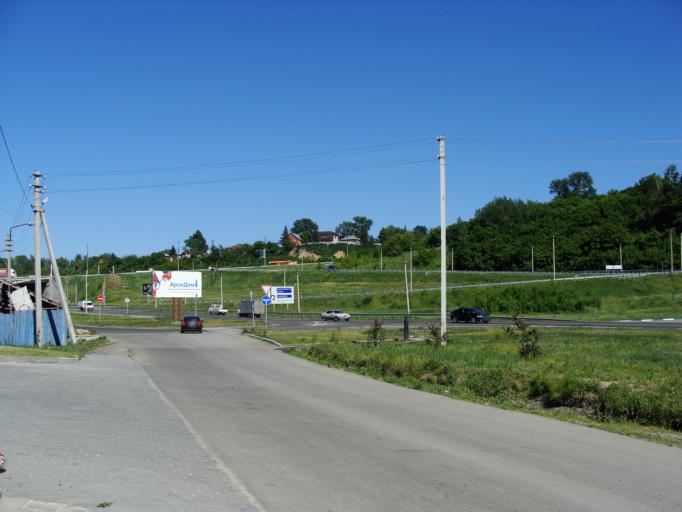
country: RU
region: Altai Krai
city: Zaton
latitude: 53.3223
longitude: 83.7829
